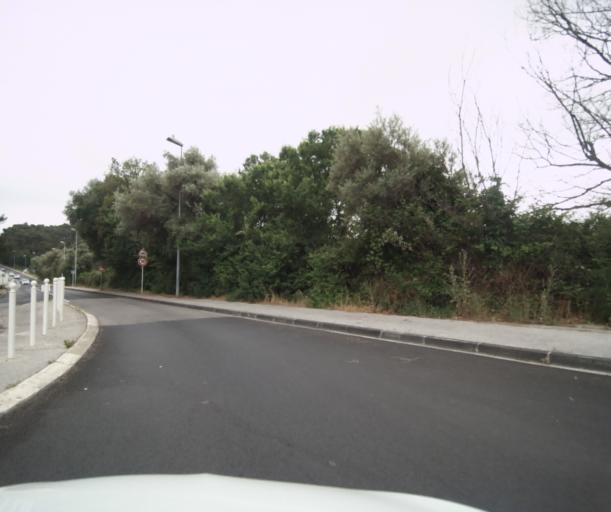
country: FR
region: Provence-Alpes-Cote d'Azur
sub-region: Departement du Var
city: Ollioules
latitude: 43.1396
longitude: 5.8828
